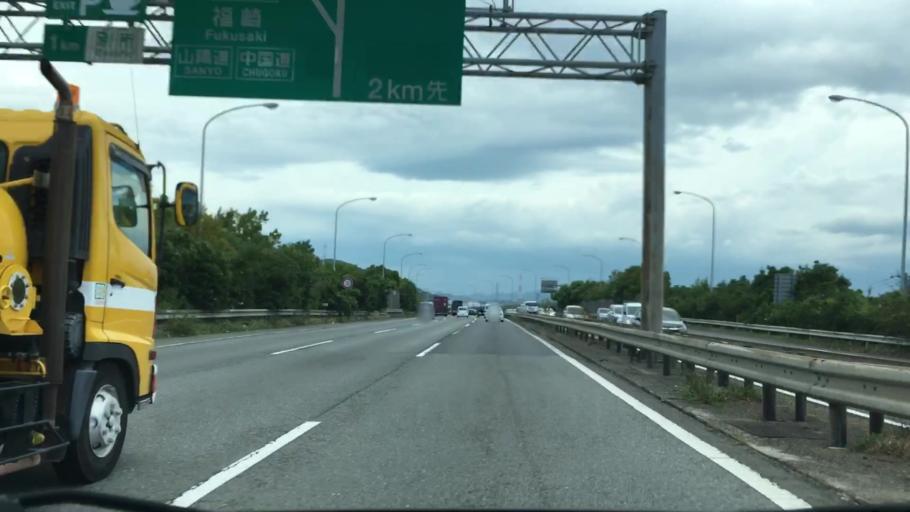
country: JP
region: Hyogo
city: Shirahamacho-usazakiminami
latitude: 34.7958
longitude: 134.7623
